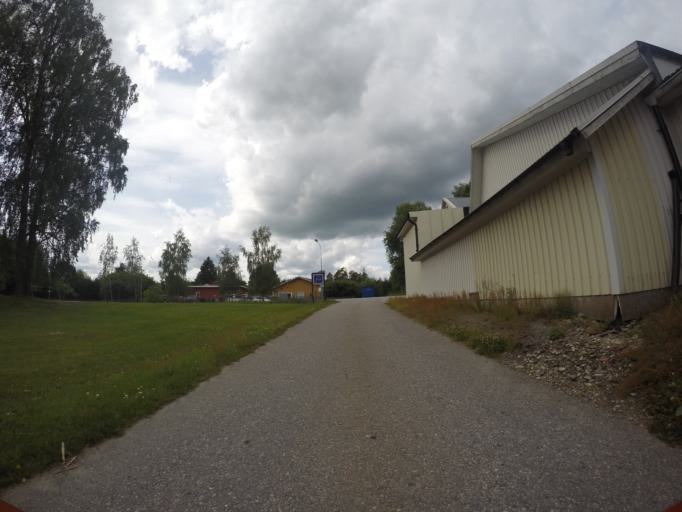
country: SE
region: Vaestra Goetaland
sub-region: Trollhattan
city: Trollhattan
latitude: 58.2270
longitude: 12.3138
